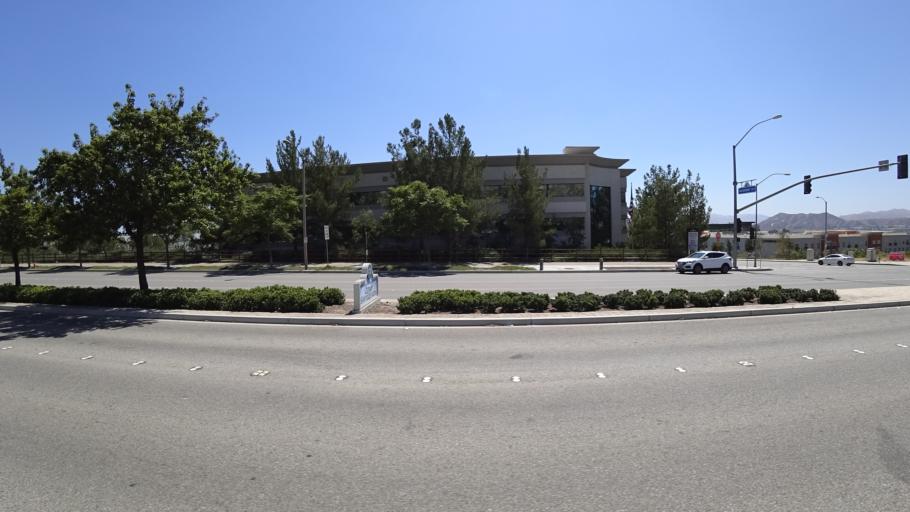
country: US
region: California
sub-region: Los Angeles County
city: Valencia
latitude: 34.4437
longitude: -118.5985
